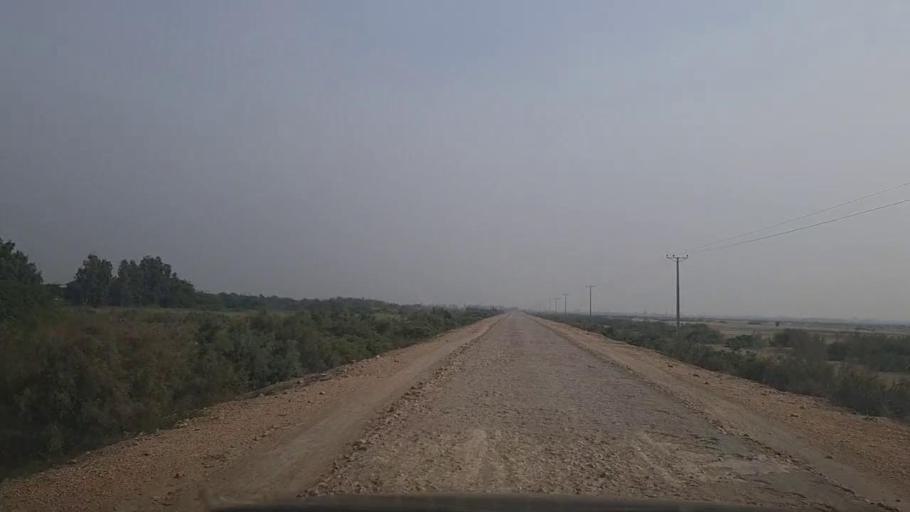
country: PK
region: Sindh
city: Mirpur Sakro
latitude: 24.4603
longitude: 67.6951
